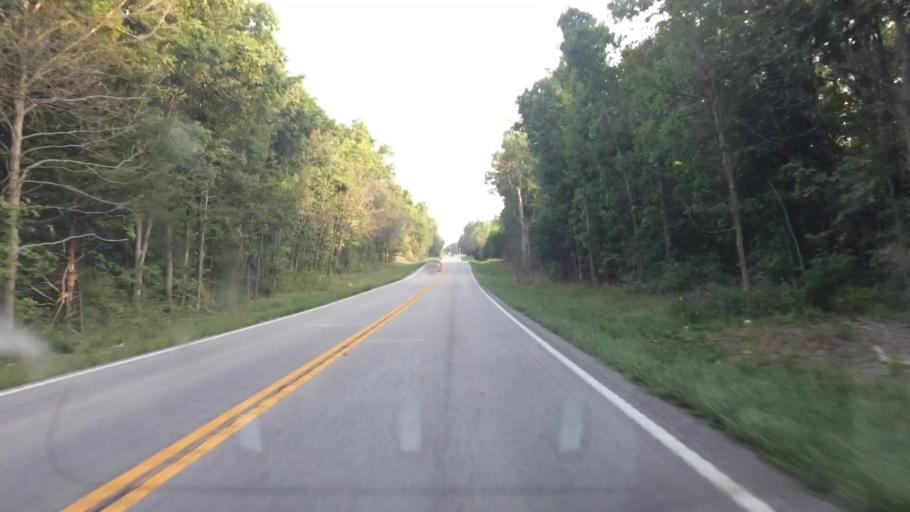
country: US
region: Missouri
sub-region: Greene County
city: Strafford
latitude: 37.1980
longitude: -93.1308
